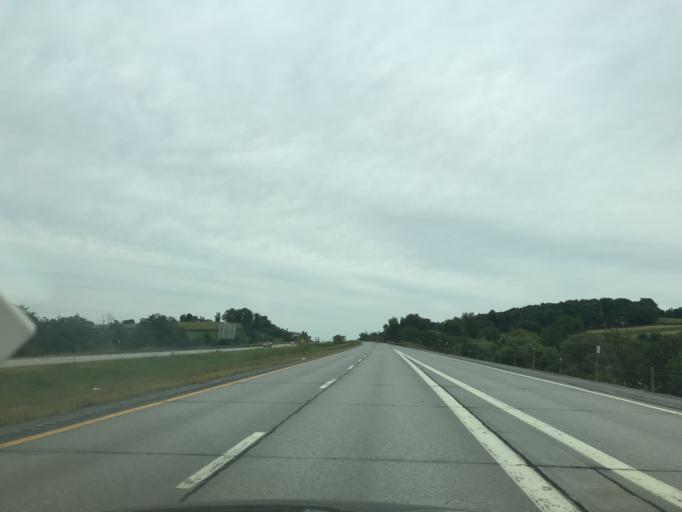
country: US
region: New York
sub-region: Schoharie County
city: Cobleskill
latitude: 42.6565
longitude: -74.5053
